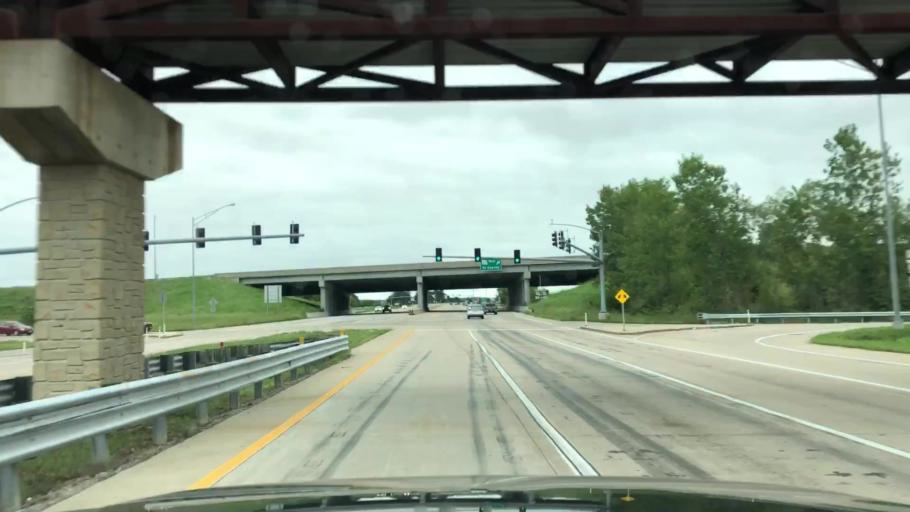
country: US
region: Missouri
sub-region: Saint Louis County
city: Maryland Heights
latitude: 38.7058
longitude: -90.5024
